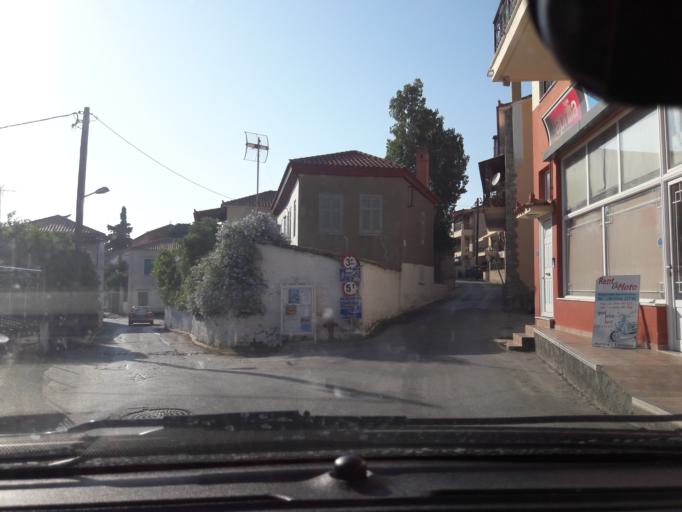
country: GR
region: North Aegean
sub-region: Nomos Lesvou
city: Myrina
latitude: 39.8724
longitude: 25.0658
